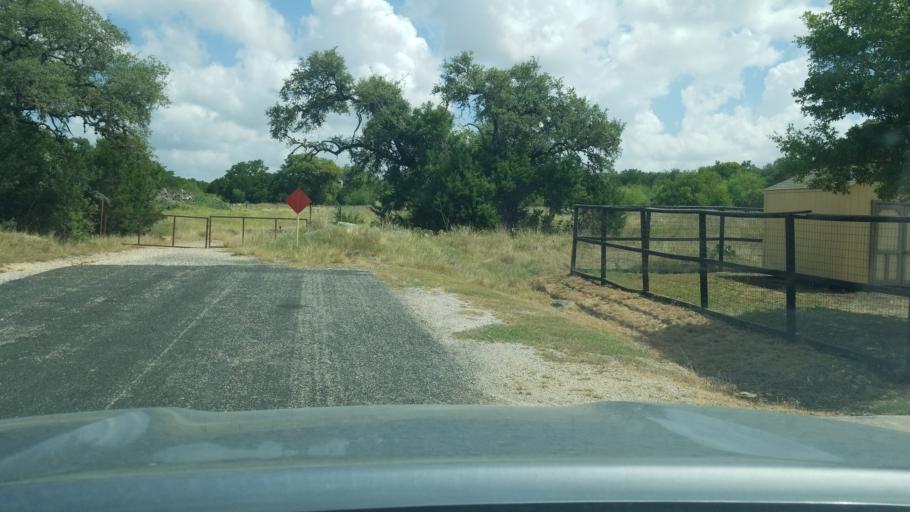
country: US
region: Texas
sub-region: Bexar County
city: Timberwood Park
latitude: 29.6938
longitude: -98.5039
